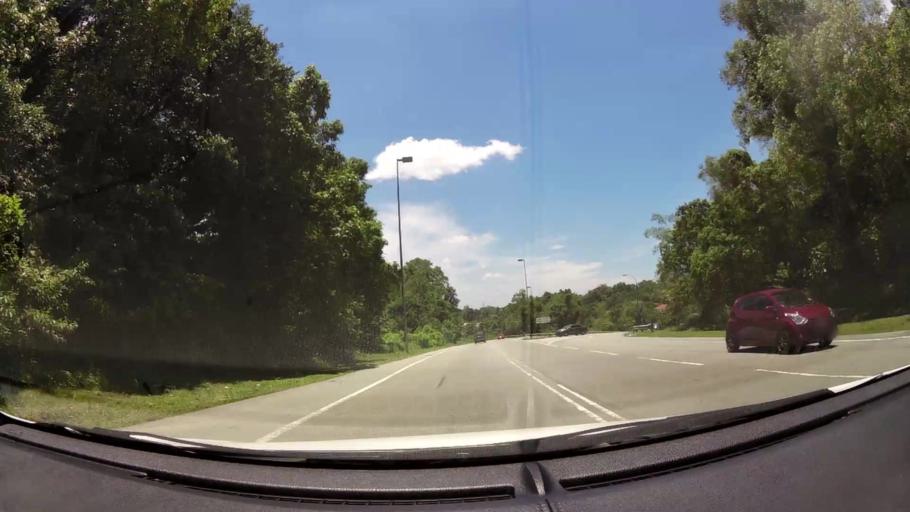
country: BN
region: Brunei and Muara
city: Bandar Seri Begawan
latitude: 4.9286
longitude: 114.9580
